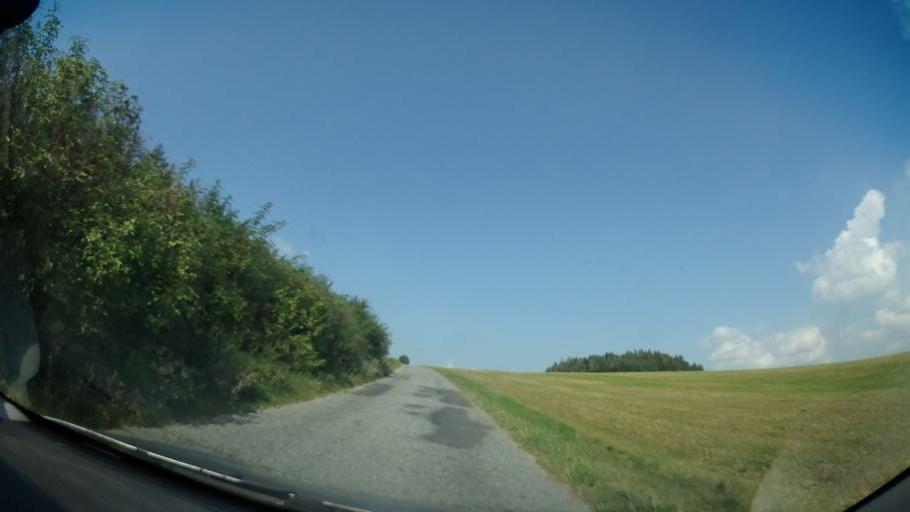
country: CZ
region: South Moravian
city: Olesnice
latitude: 49.5511
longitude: 16.3553
